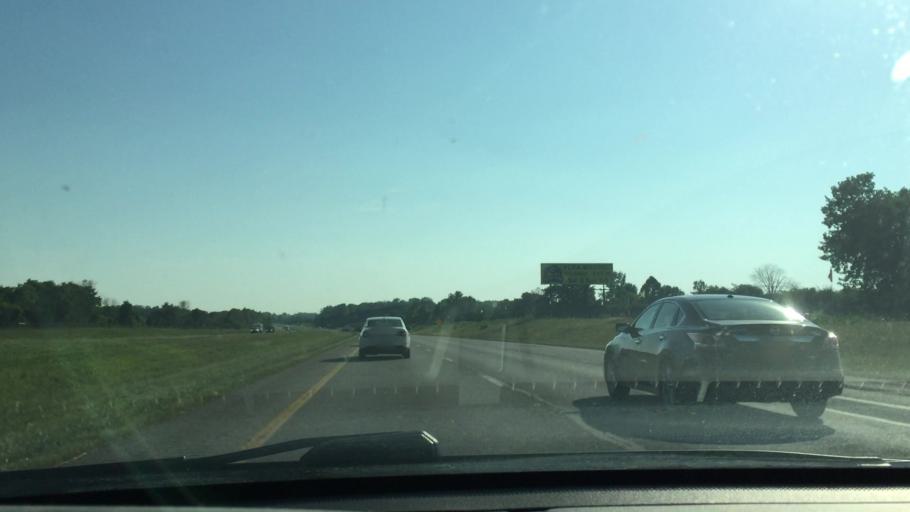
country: US
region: Ohio
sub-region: Clinton County
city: Wilmington
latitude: 39.4839
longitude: -83.9486
